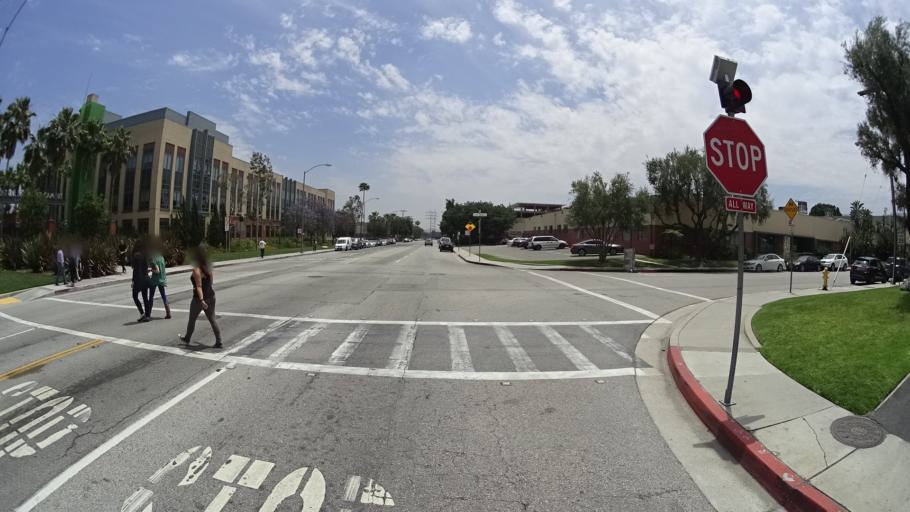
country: US
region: California
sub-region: Los Angeles County
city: North Glendale
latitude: 34.1597
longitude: -118.2870
